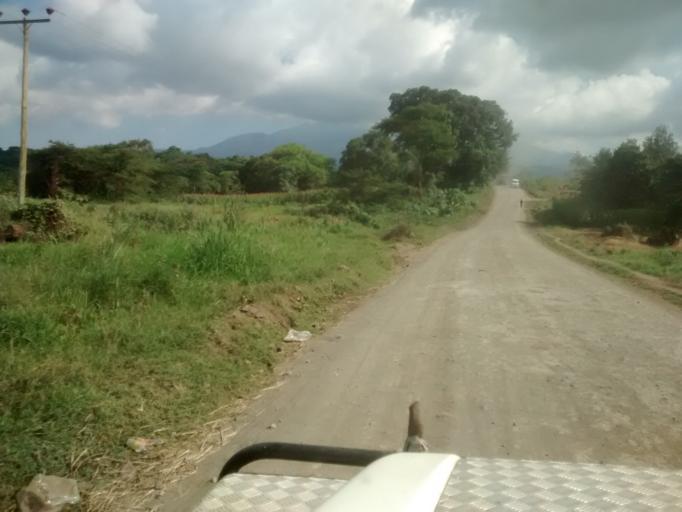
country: TZ
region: Arusha
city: Usa River
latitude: -3.3677
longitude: 36.8463
